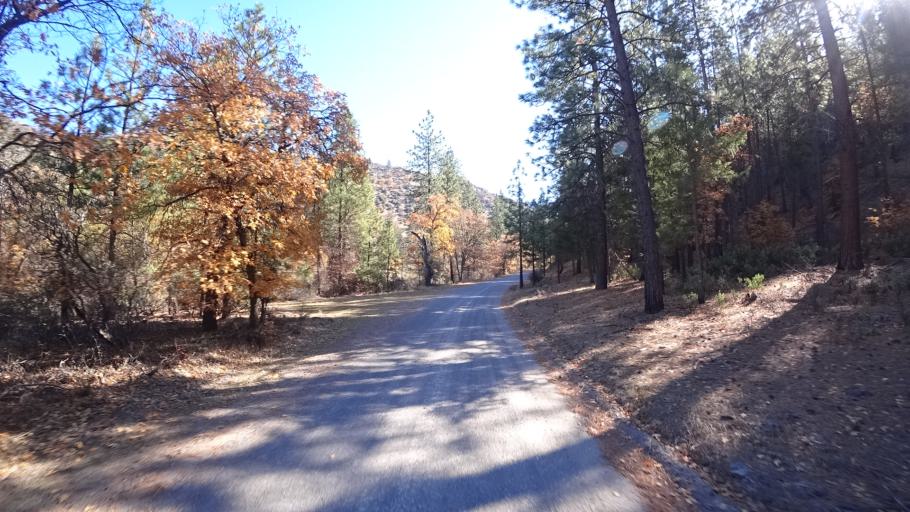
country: US
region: California
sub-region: Siskiyou County
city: Yreka
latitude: 41.8540
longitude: -122.6971
